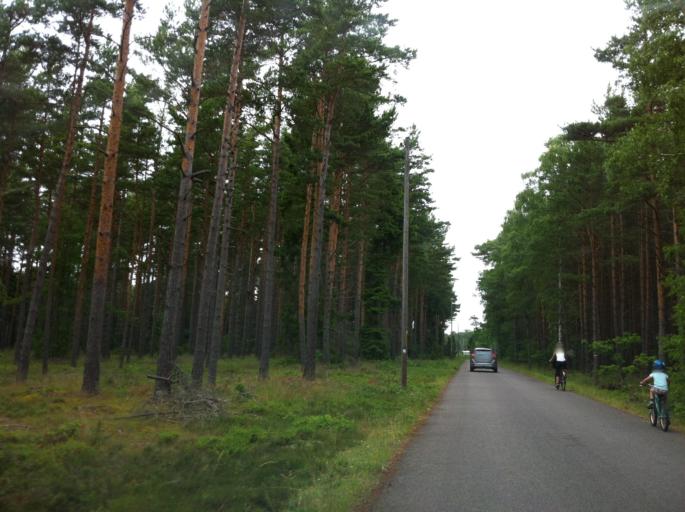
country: SE
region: Kalmar
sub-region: Vasterviks Kommun
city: Vaestervik
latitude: 57.3322
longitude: 17.1100
